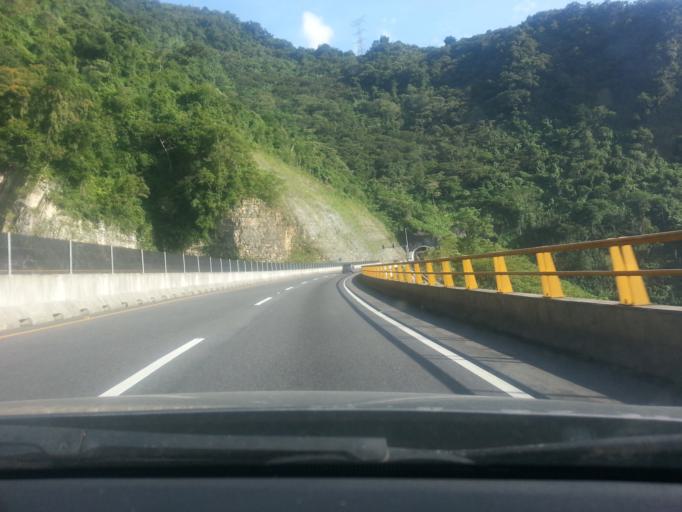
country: MX
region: Puebla
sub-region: Xicotepec
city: San Lorenzo
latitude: 20.3189
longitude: -97.9639
